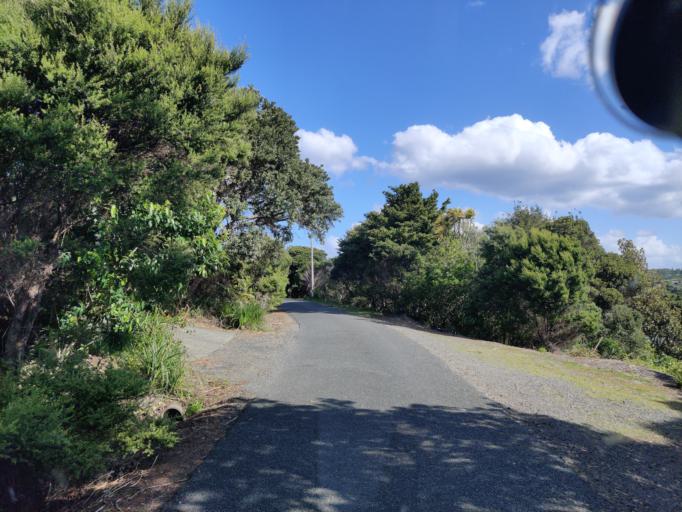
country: NZ
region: Northland
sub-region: Whangarei
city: Ngunguru
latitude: -35.6093
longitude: 174.5294
